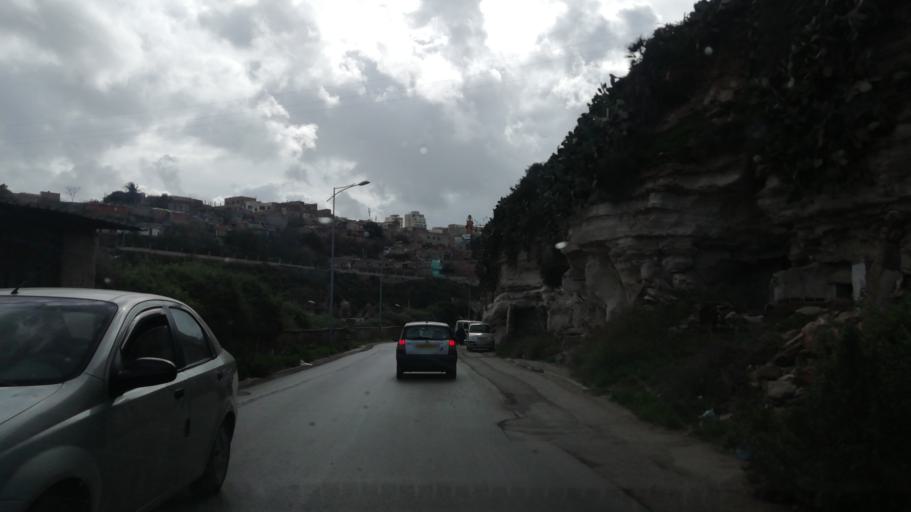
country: DZ
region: Oran
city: Oran
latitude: 35.6952
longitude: -0.6595
